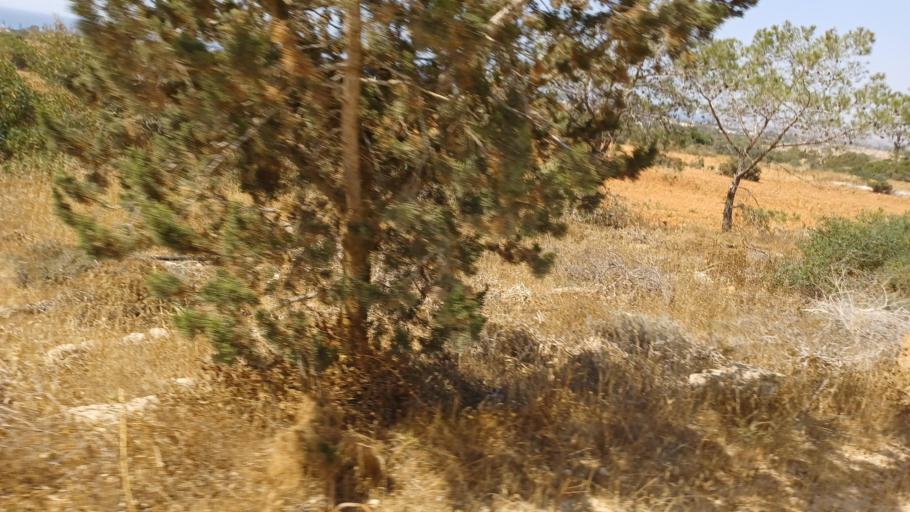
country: CY
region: Ammochostos
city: Ayia Napa
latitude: 35.0027
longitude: 33.9707
